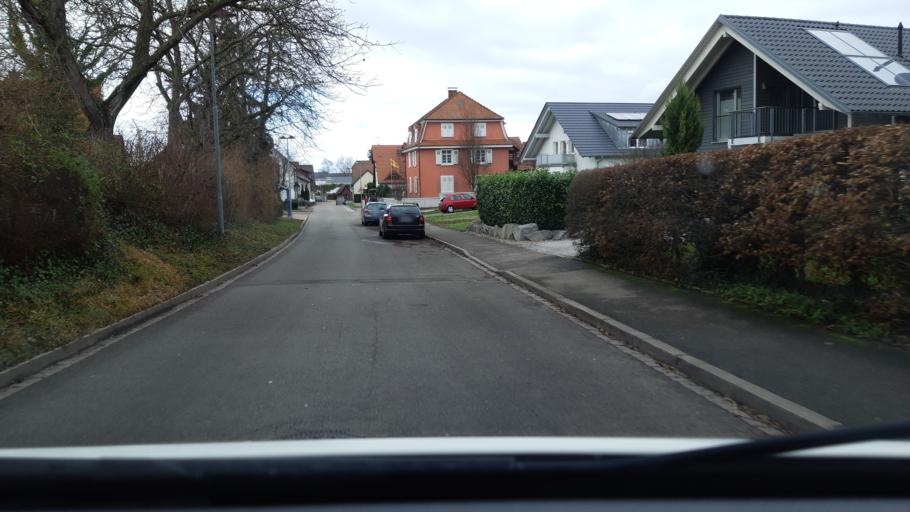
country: DE
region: Baden-Wuerttemberg
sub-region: Freiburg Region
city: Pfaffenweiler
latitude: 47.9367
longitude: 7.7281
